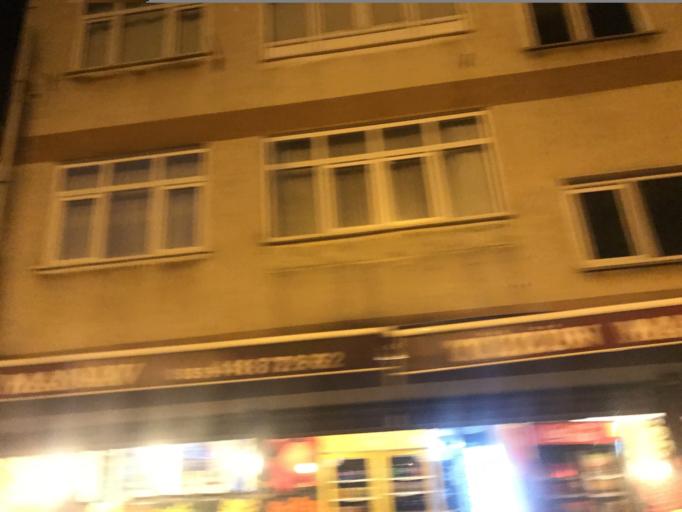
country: TR
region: Istanbul
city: Maltepe
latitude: 40.9224
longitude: 29.1413
